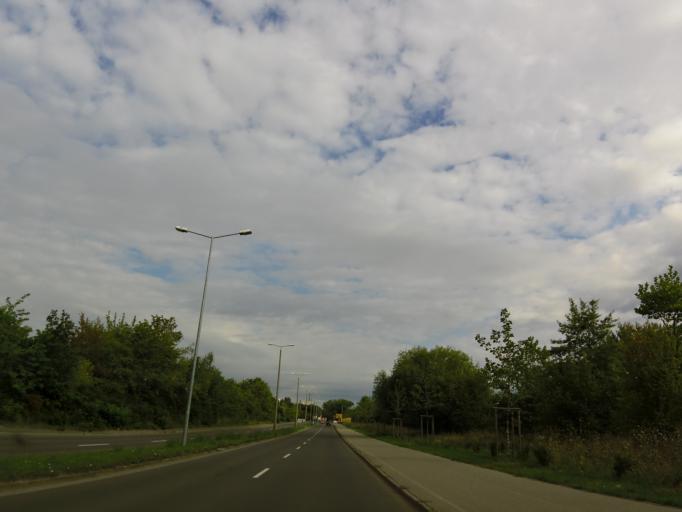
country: DE
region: Saxony
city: Leipzig
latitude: 51.3236
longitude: 12.3070
